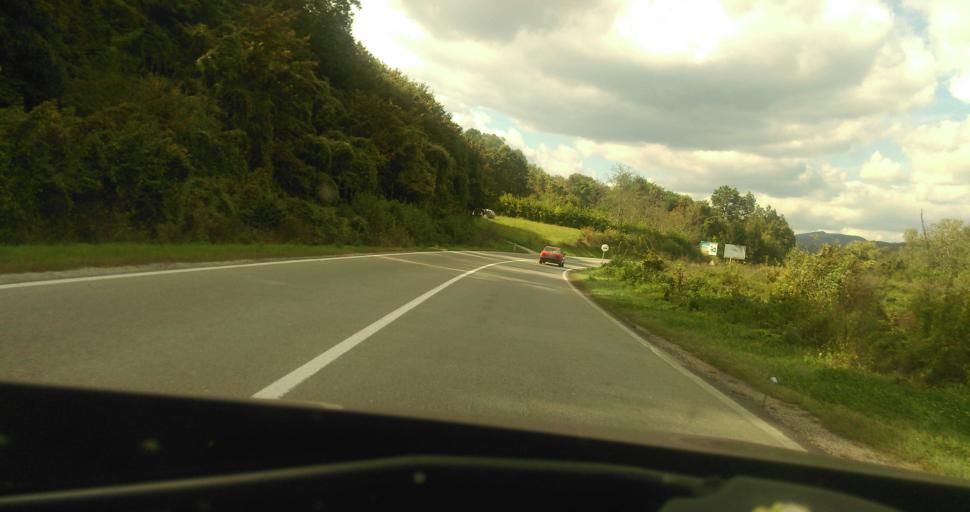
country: RS
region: Central Serbia
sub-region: Moravicki Okrug
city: Cacak
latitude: 43.8966
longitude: 20.2838
